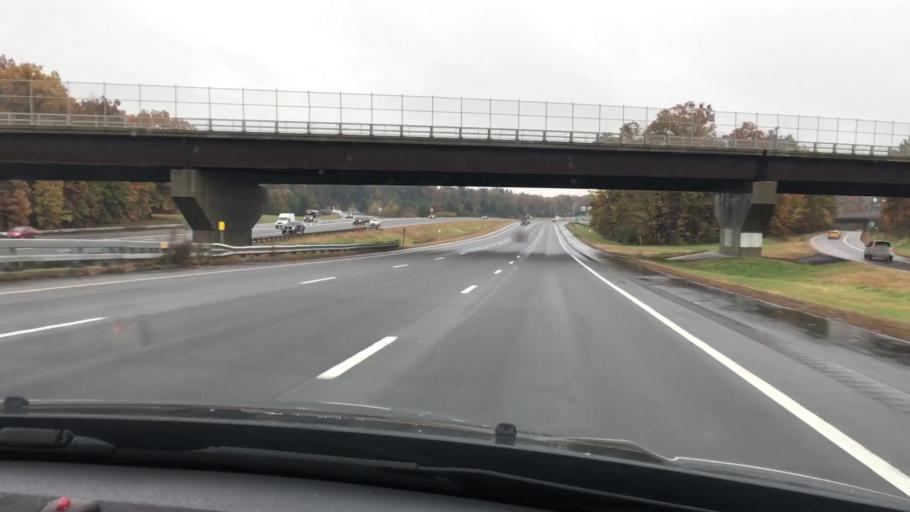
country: US
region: New Hampshire
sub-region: Hillsborough County
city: Hudson
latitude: 42.7229
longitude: -71.4502
